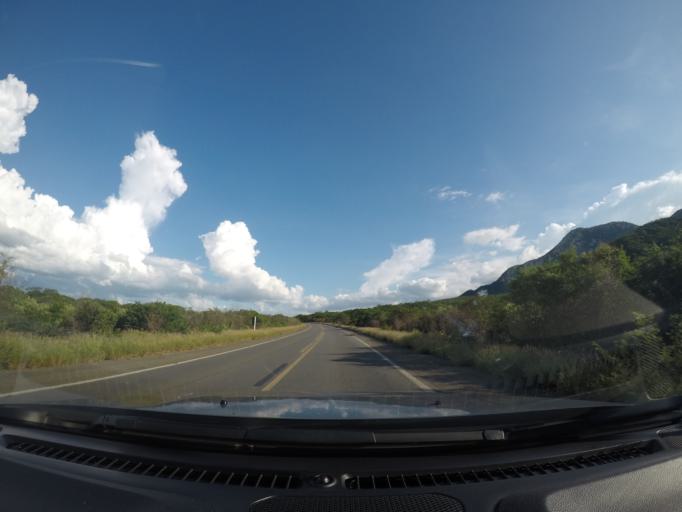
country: BR
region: Bahia
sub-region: Oliveira Dos Brejinhos
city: Oliveira dos Brejinhos
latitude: -12.0659
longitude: -42.9587
